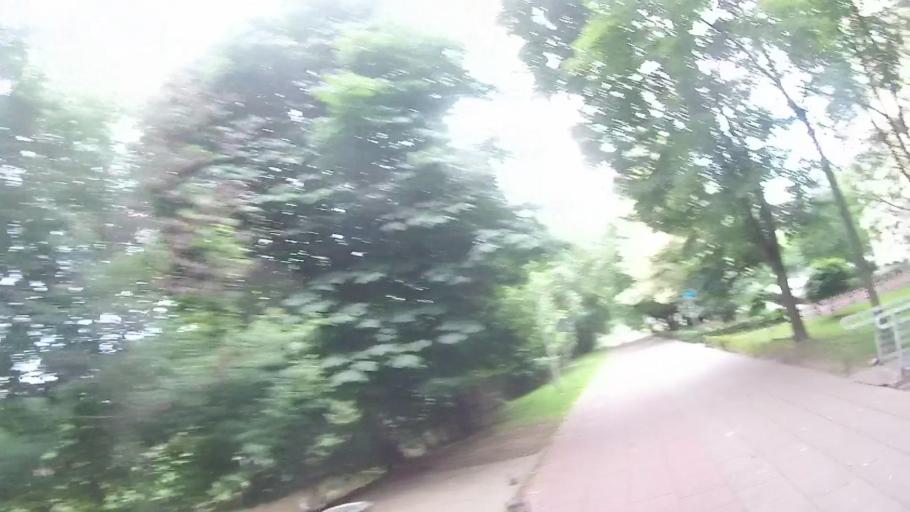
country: PL
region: Masovian Voivodeship
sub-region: Warszawa
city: Praga Poludnie
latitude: 52.2377
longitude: 21.0659
